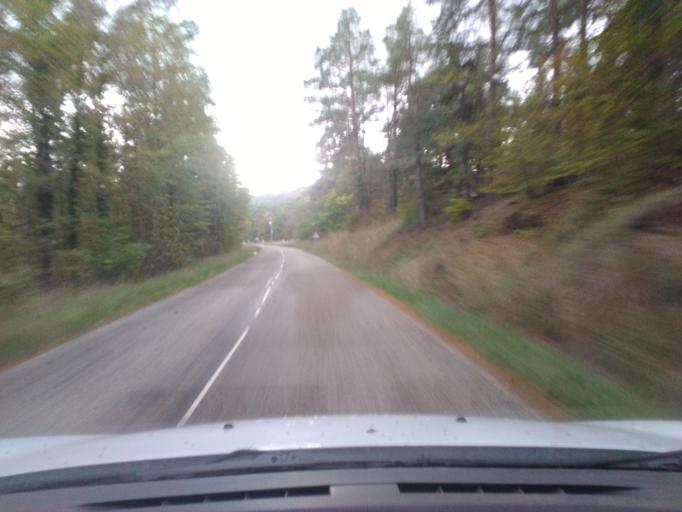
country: FR
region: Lorraine
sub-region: Departement des Vosges
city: Saint-Die-des-Vosges
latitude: 48.3150
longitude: 6.9654
